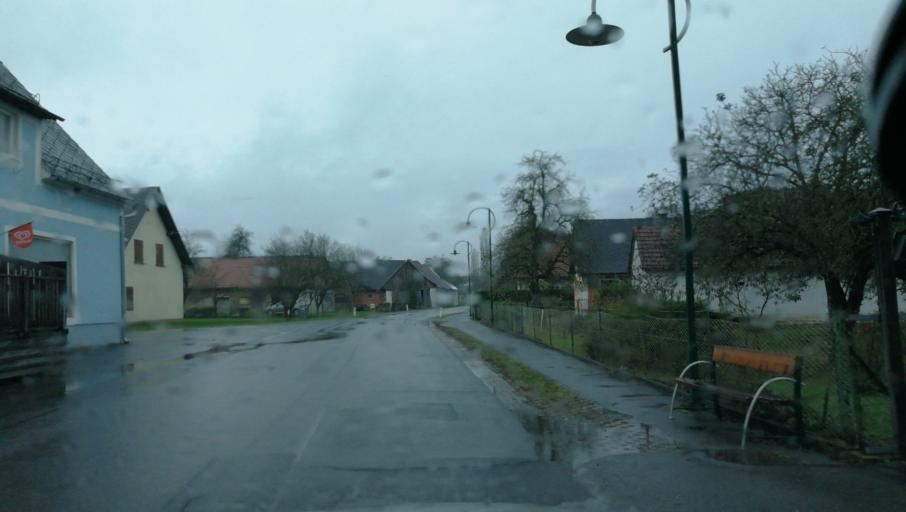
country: AT
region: Styria
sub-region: Politischer Bezirk Suedoststeiermark
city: Weinburg am Sassbach
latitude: 46.7352
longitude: 15.7169
